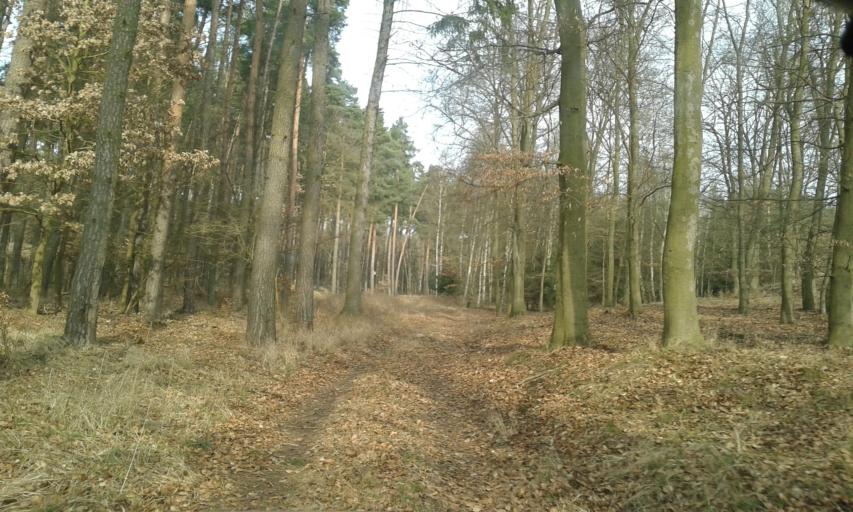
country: PL
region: West Pomeranian Voivodeship
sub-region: Powiat mysliborski
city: Barlinek
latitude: 53.0854
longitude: 15.2133
